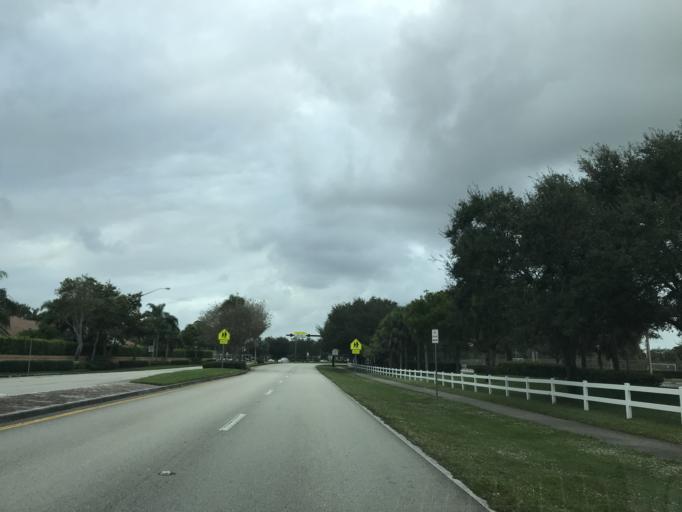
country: US
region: Florida
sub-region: Broward County
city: Coral Springs
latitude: 26.2981
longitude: -80.2649
